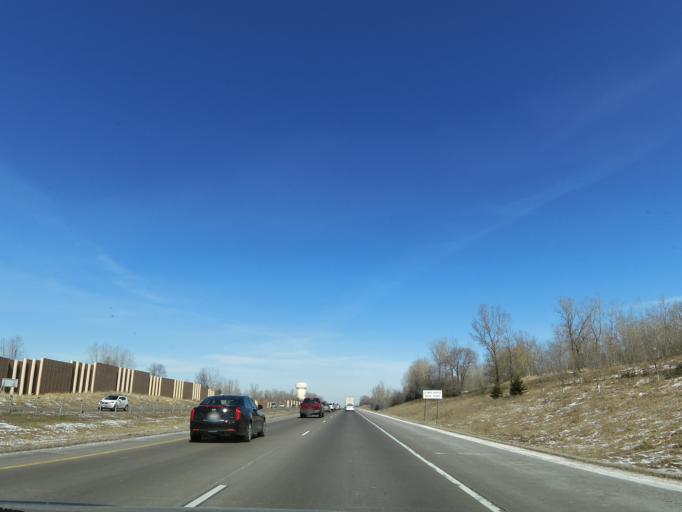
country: US
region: Minnesota
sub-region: Washington County
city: Oakdale
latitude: 44.9730
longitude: -92.9588
